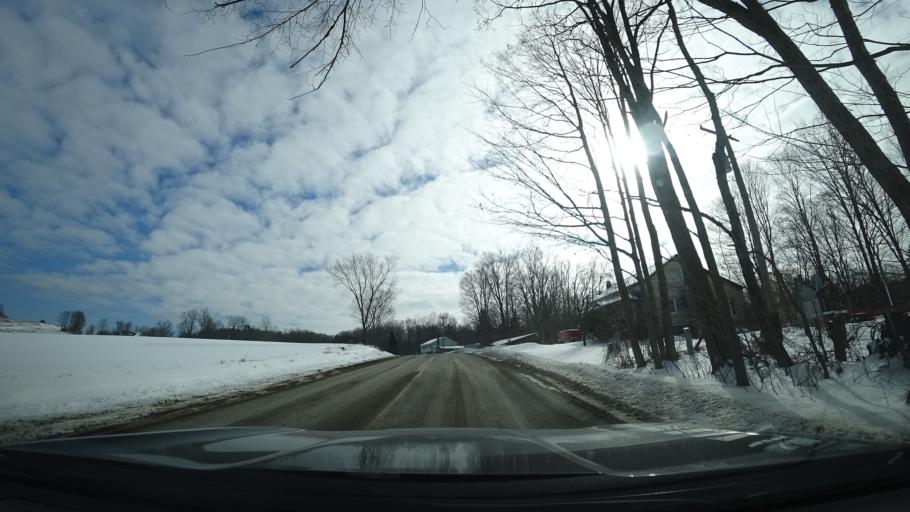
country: US
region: New York
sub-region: Washington County
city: Fort Edward
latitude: 43.2470
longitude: -73.4629
